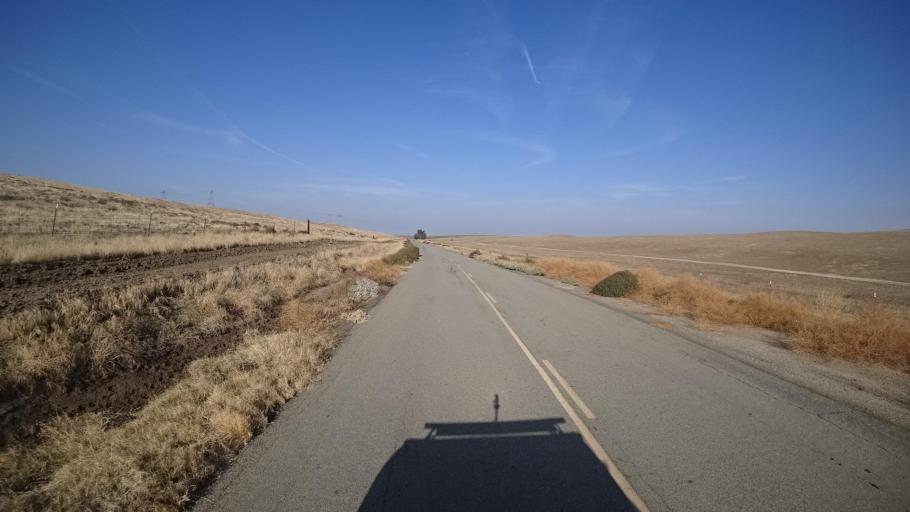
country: US
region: California
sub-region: Tulare County
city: Richgrove
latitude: 35.6359
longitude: -119.0369
